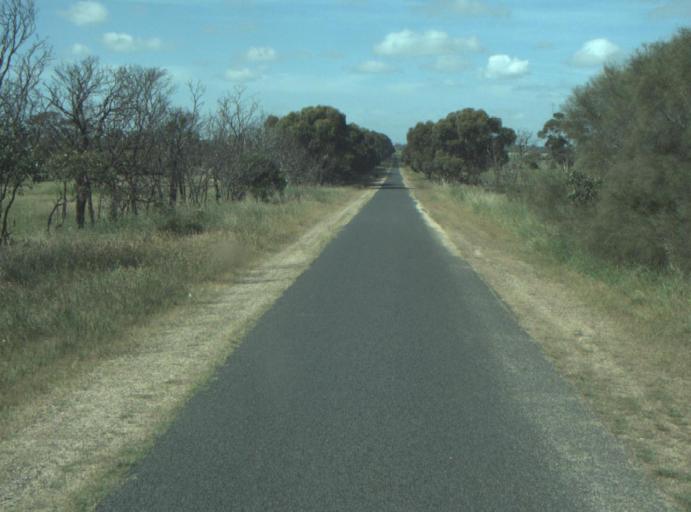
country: AU
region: Victoria
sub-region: Greater Geelong
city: Lara
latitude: -37.9701
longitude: 144.4246
